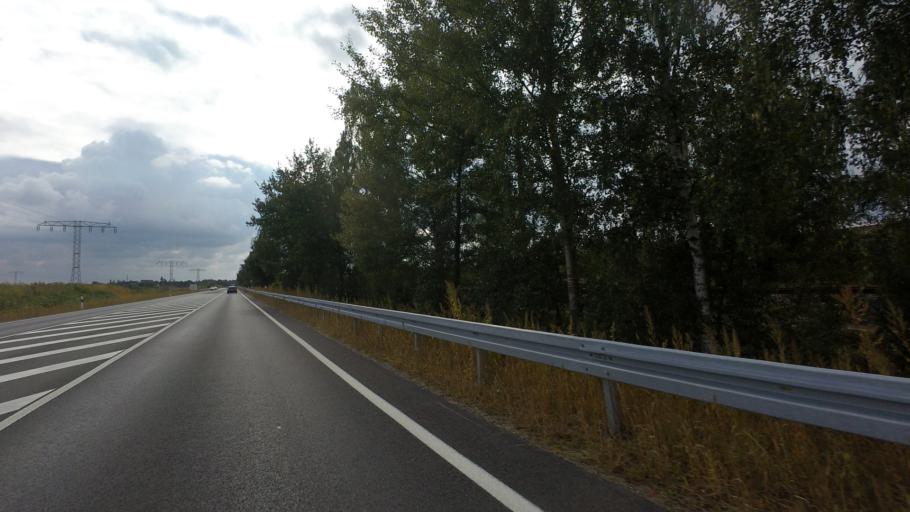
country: DE
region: Brandenburg
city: Grossraschen
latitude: 51.5626
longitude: 14.0635
